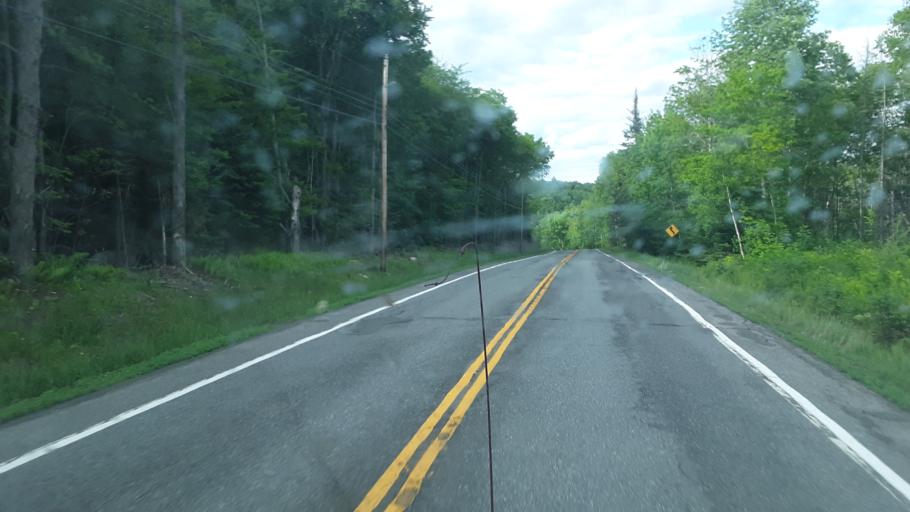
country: US
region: Maine
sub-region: Penobscot County
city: Patten
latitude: 46.1262
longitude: -68.3919
